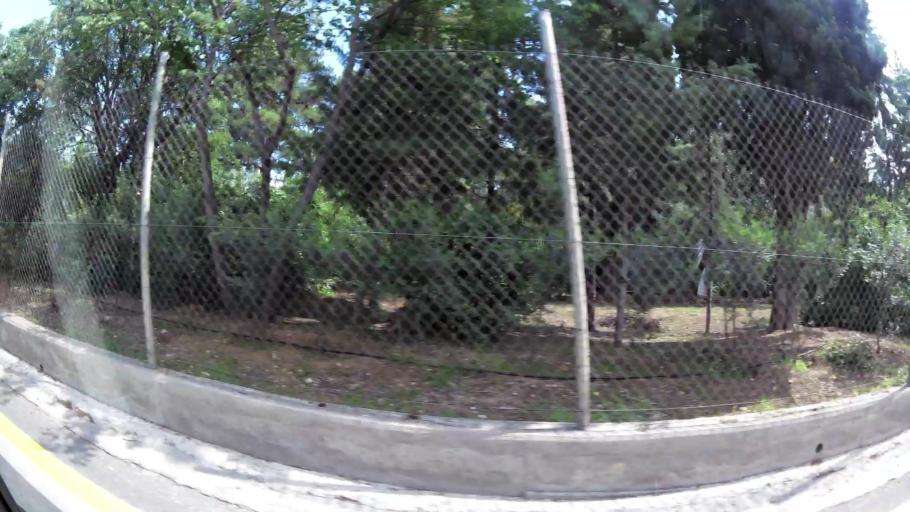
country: GR
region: Central Macedonia
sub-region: Nomos Thessalonikis
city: Pylaia
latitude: 40.5964
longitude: 23.0034
